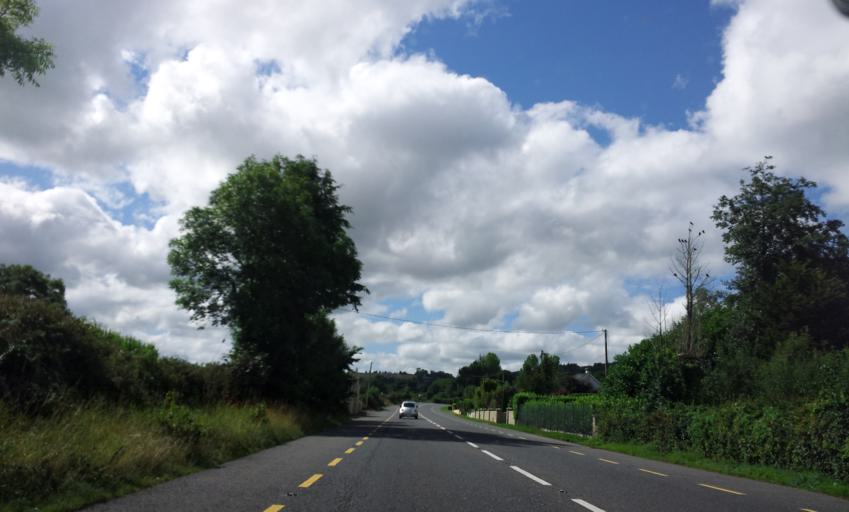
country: IE
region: Munster
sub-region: County Cork
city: Killumney
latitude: 51.8808
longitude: -8.6580
